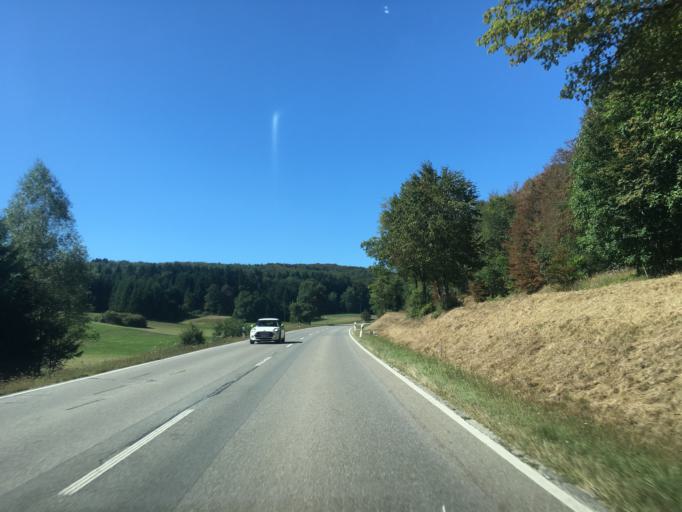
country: DE
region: Baden-Wuerttemberg
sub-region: Tuebingen Region
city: Pfullingen
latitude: 48.3969
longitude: 9.2206
